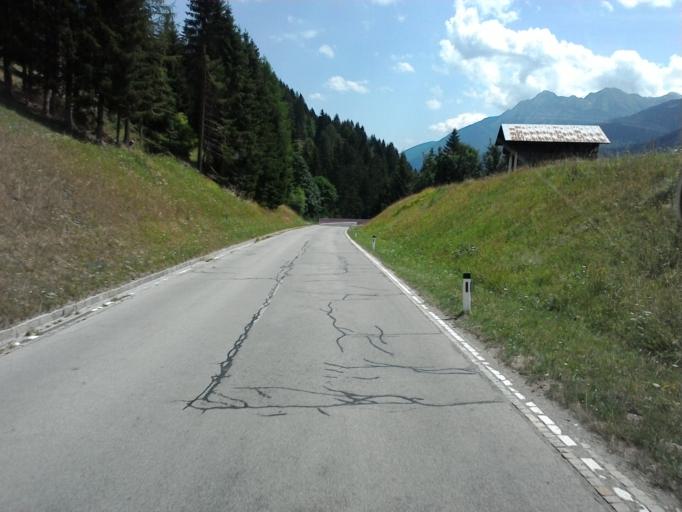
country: AT
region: Tyrol
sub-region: Politischer Bezirk Lienz
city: Untertilliach
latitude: 46.6971
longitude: 12.7990
